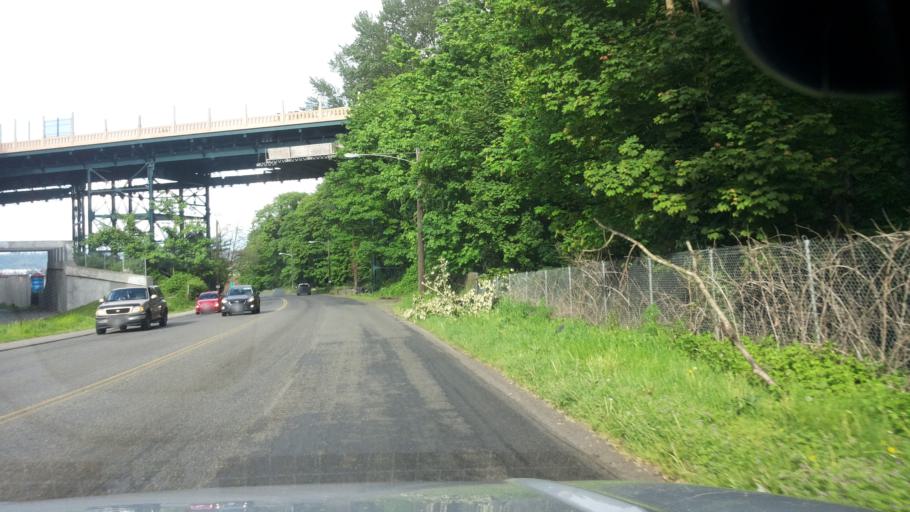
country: US
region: Washington
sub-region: Pierce County
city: Tacoma
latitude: 47.2339
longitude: -122.4419
